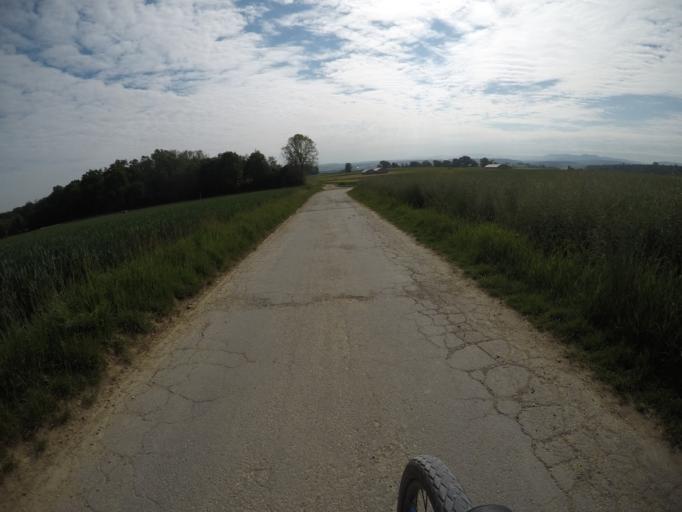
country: DE
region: Baden-Wuerttemberg
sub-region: Regierungsbezirk Stuttgart
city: Denkendorf
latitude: 48.6645
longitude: 9.3216
